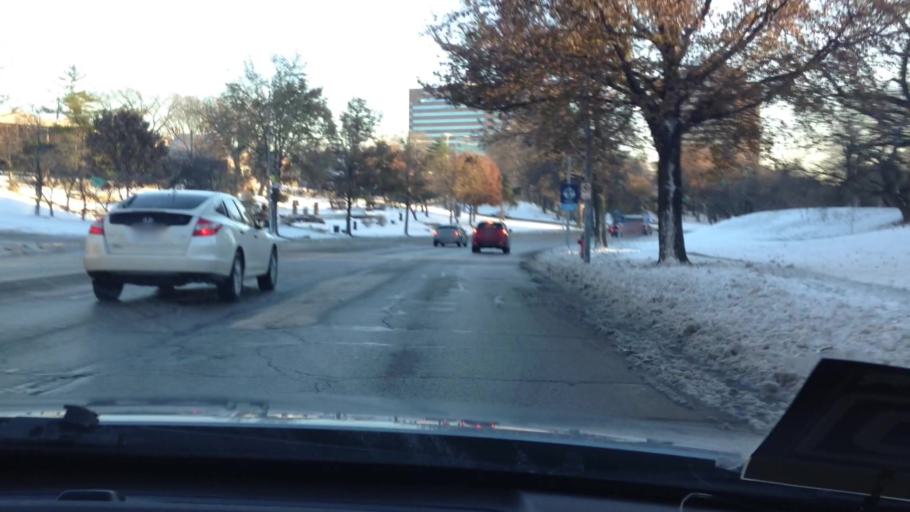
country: US
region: Kansas
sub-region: Johnson County
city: Westwood
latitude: 39.0510
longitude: -94.5888
